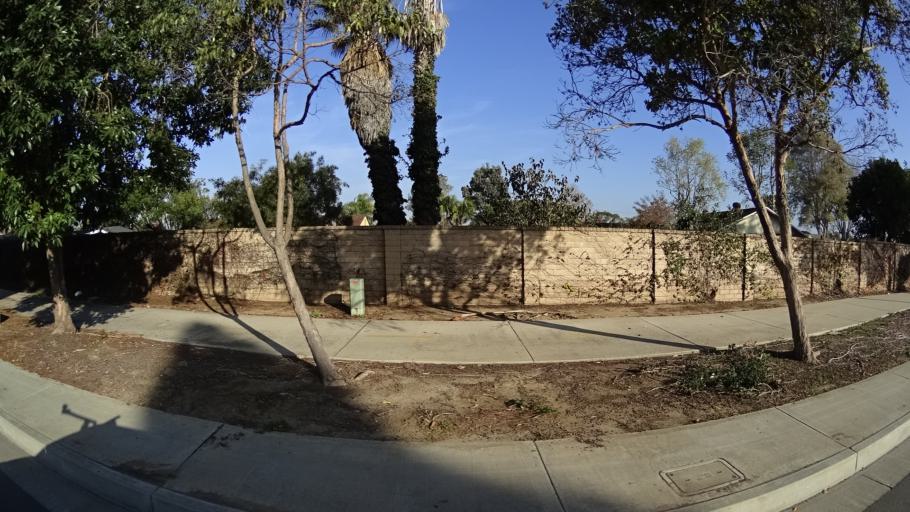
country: US
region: California
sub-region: Orange County
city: Costa Mesa
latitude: 33.6527
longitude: -117.9343
